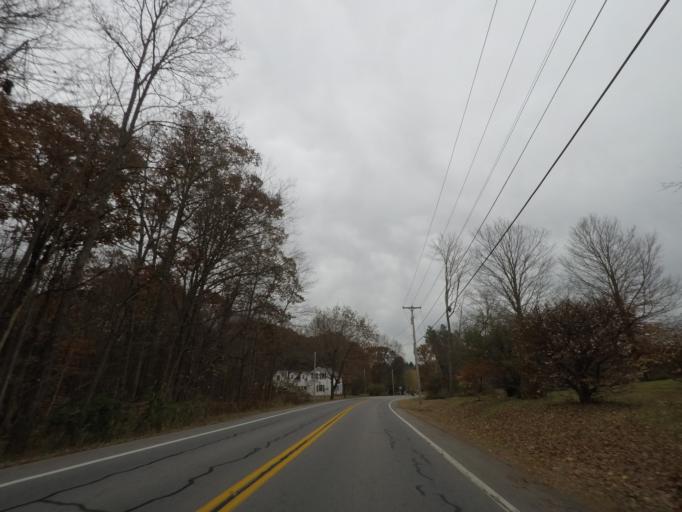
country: US
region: New York
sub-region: Schenectady County
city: Niskayuna
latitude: 42.8101
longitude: -73.8259
